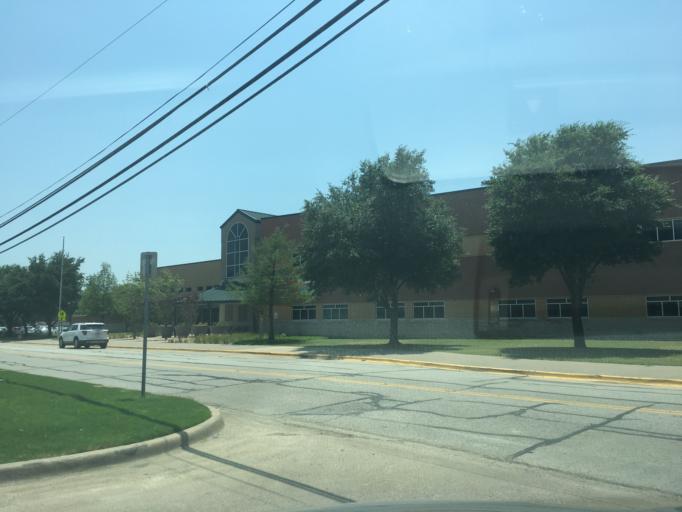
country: US
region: Texas
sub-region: Dallas County
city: Carrollton
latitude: 32.9384
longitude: -96.8799
